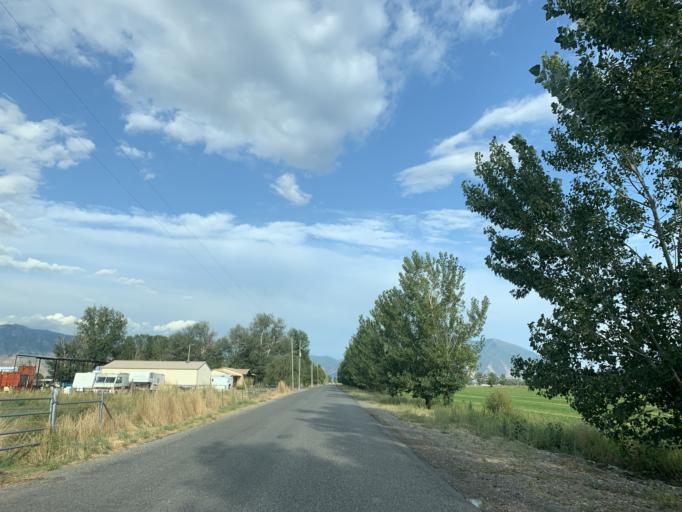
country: US
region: Utah
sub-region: Utah County
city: Benjamin
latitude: 40.1292
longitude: -111.7465
